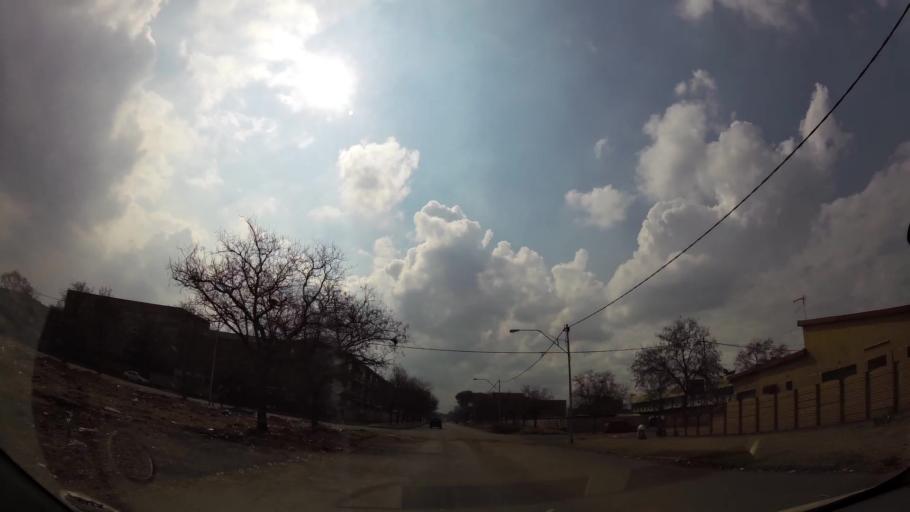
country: ZA
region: Gauteng
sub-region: Sedibeng District Municipality
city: Vereeniging
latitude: -26.6741
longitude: 27.9252
